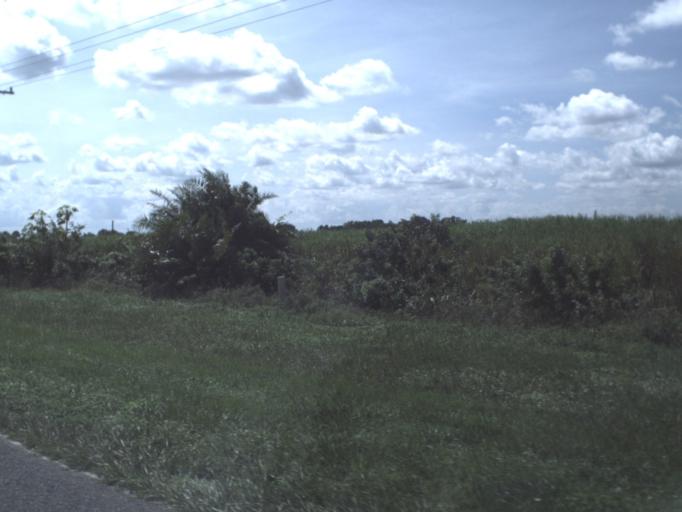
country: US
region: Florida
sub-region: Glades County
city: Moore Haven
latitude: 26.8145
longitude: -81.0827
